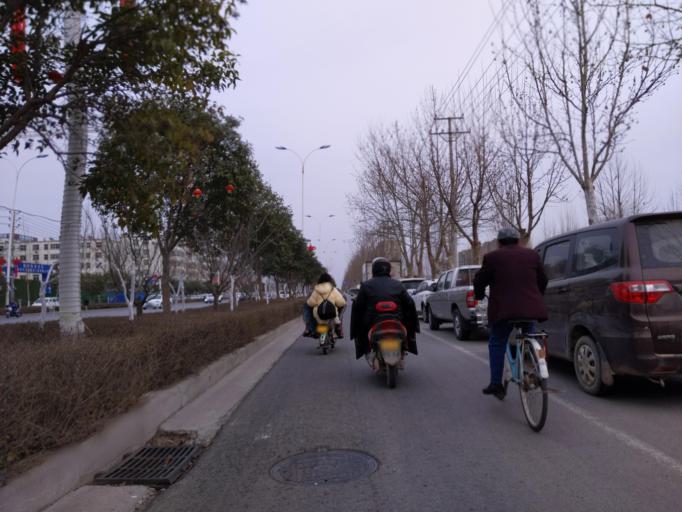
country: CN
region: Henan Sheng
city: Zhongyuanlu
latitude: 35.7569
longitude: 115.0790
